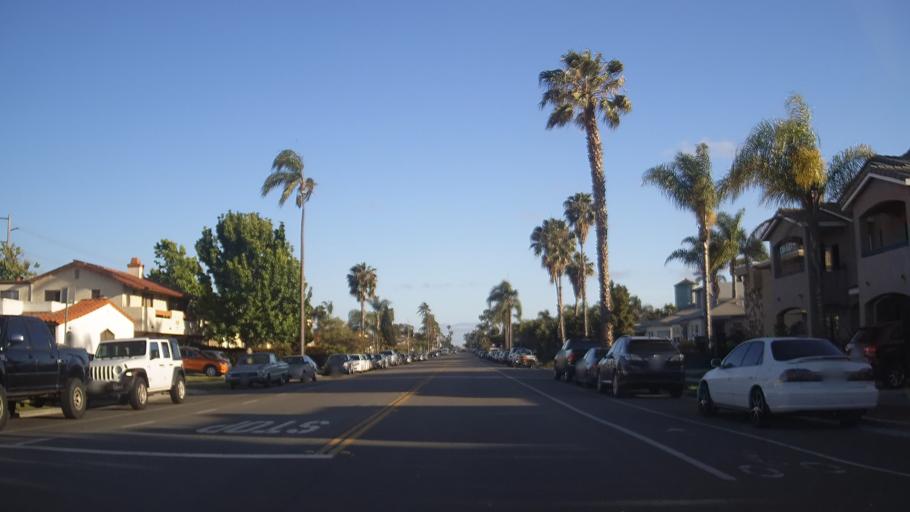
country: US
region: California
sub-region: San Diego County
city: San Diego
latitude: 32.7591
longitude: -117.1327
